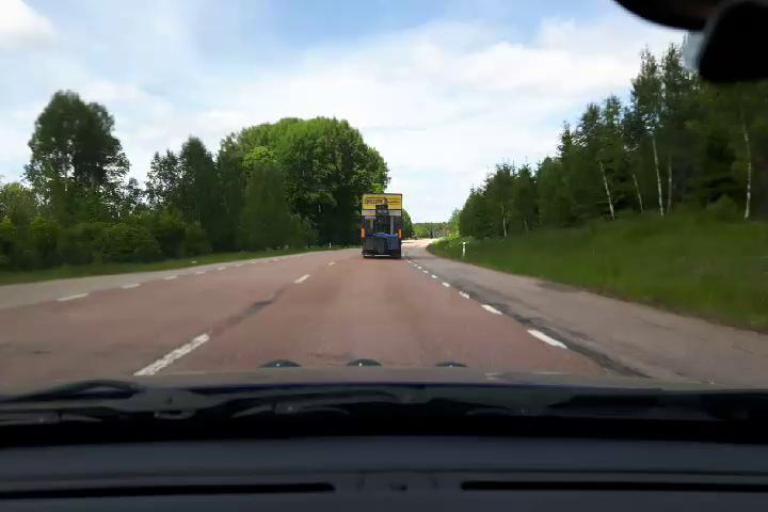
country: SE
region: Uppsala
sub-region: Osthammars Kommun
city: Bjorklinge
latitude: 60.1500
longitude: 17.4939
